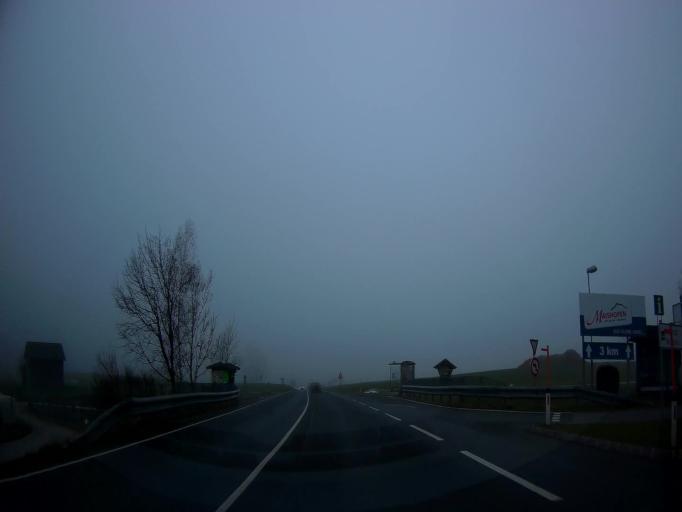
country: AT
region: Salzburg
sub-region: Politischer Bezirk Zell am See
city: Maishofen
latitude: 47.3886
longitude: 12.8039
